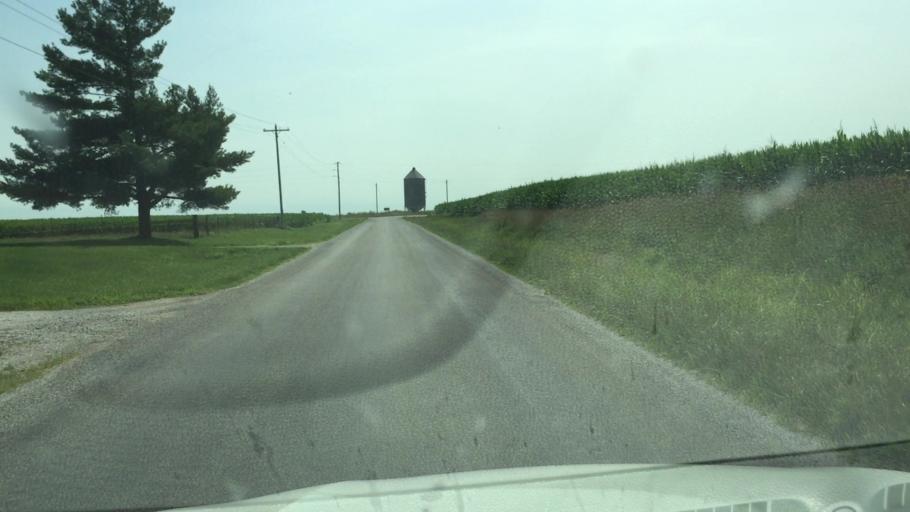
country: US
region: Illinois
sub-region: Hancock County
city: Nauvoo
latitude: 40.5112
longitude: -91.3299
